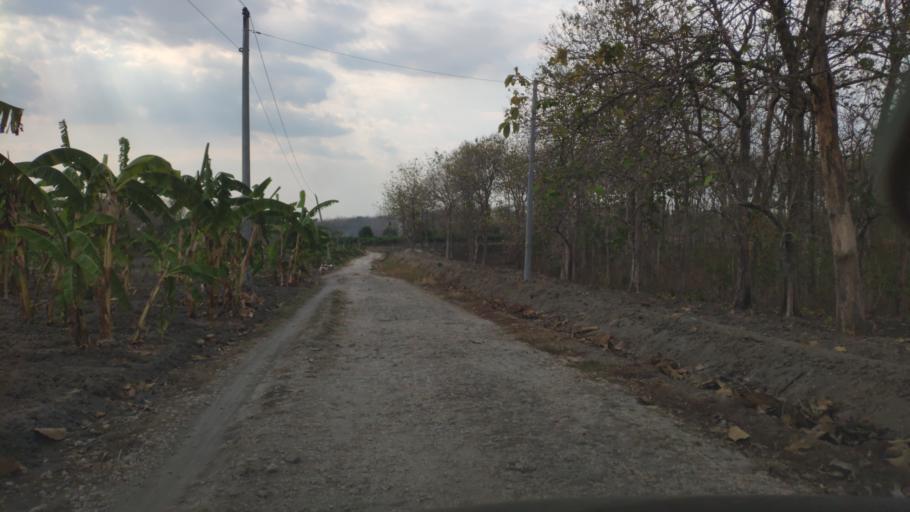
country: ID
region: Central Java
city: Randublatung
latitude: -7.2877
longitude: 111.3289
